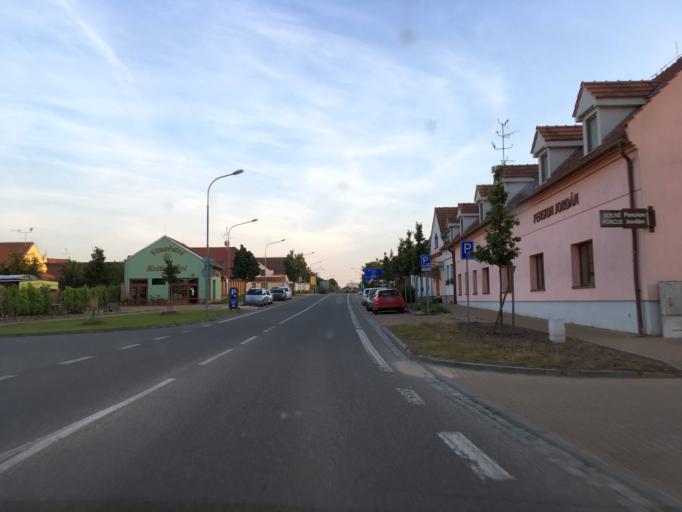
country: CZ
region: South Moravian
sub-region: Okres Breclav
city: Lednice
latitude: 48.8013
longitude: 16.8021
